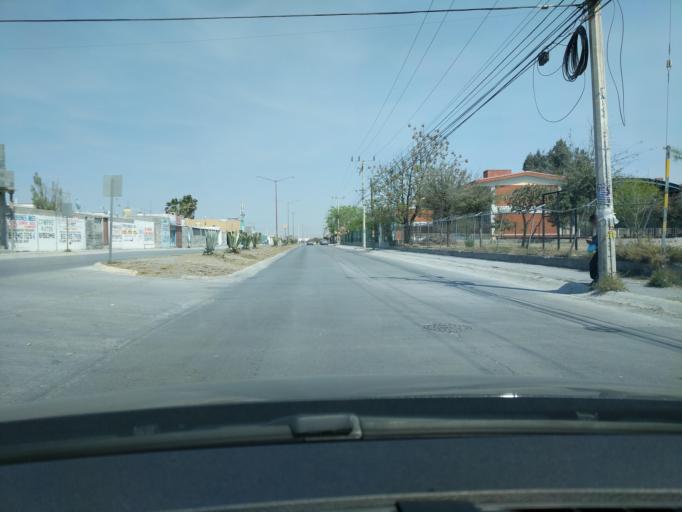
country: MX
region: Nuevo Leon
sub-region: Garcia
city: Valle de Lincoln
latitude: 25.7916
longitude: -100.4836
